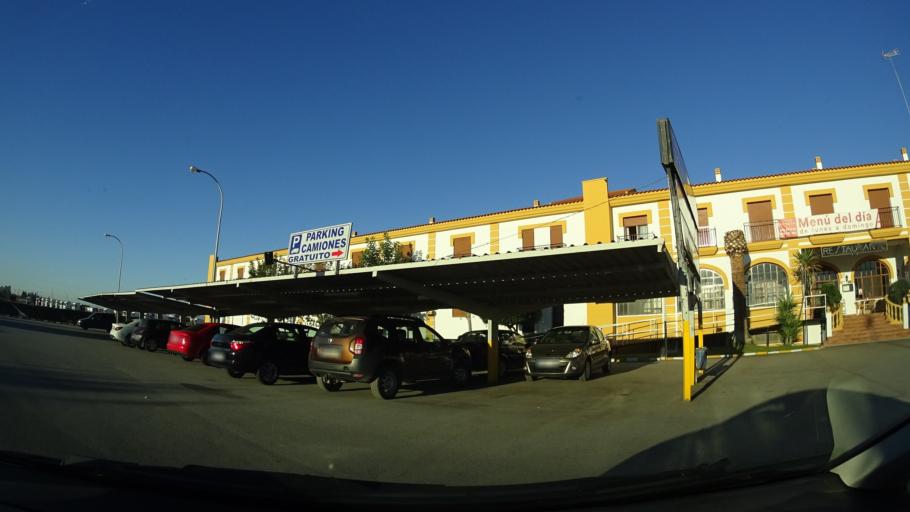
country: ES
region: Extremadura
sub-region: Provincia de Badajoz
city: Almendralejo
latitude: 38.7095
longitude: -6.4002
